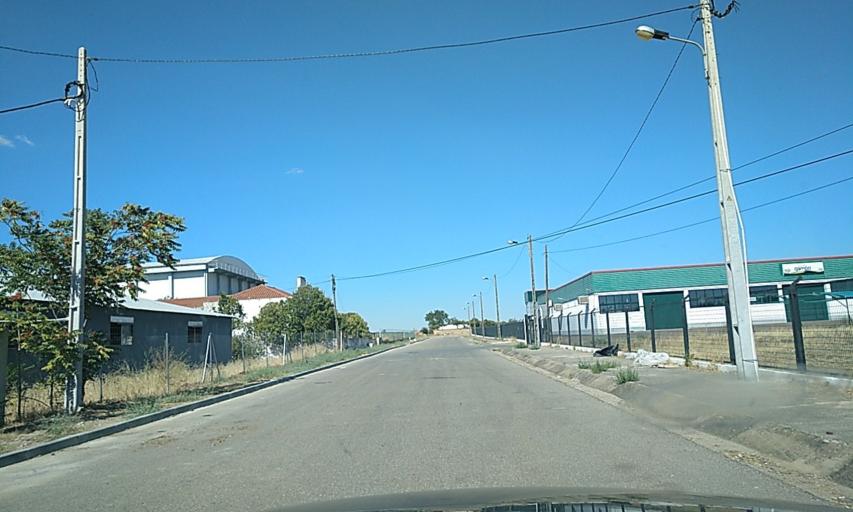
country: PT
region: Portalegre
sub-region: Campo Maior
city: Campo Maior
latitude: 39.0232
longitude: -7.0599
